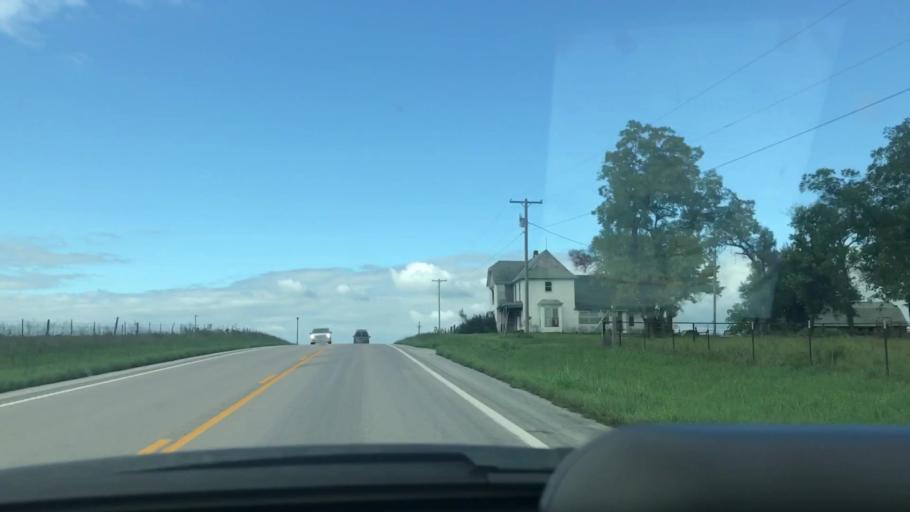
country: US
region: Missouri
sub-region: Hickory County
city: Hermitage
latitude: 37.9538
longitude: -93.2073
